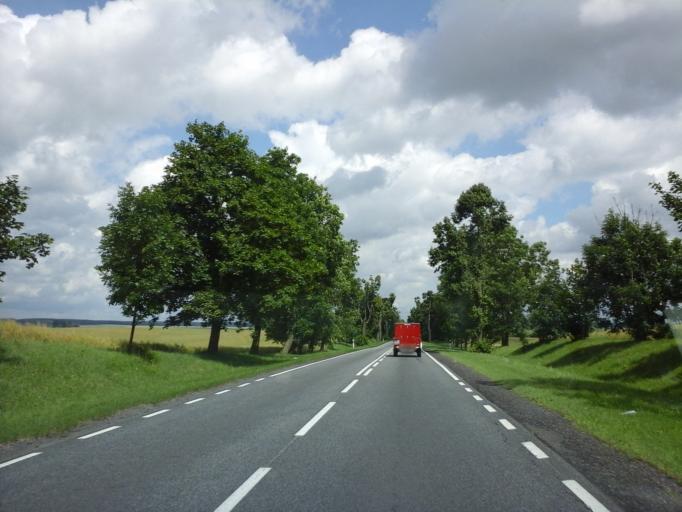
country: PL
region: Lubusz
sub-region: Powiat strzelecko-drezdenecki
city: Strzelce Krajenskie
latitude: 52.8893
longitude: 15.5613
